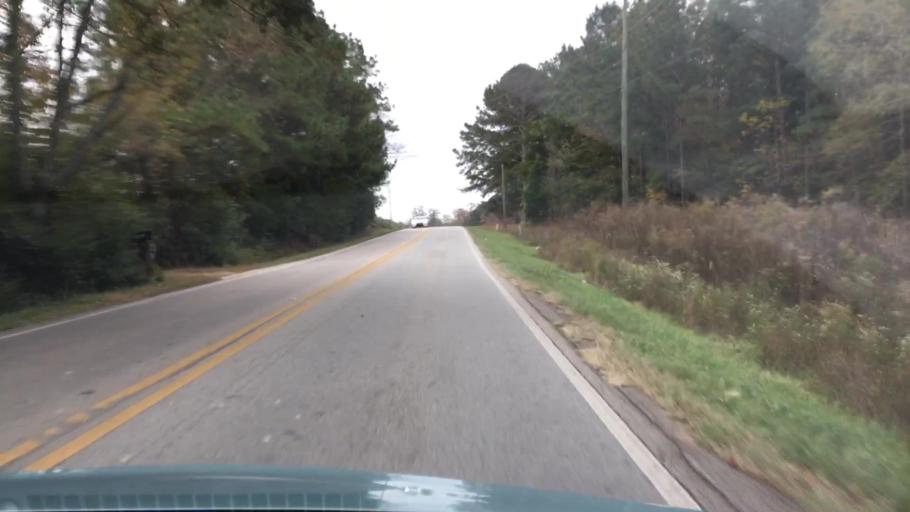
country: US
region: Georgia
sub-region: Henry County
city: McDonough
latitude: 33.5047
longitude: -84.1047
